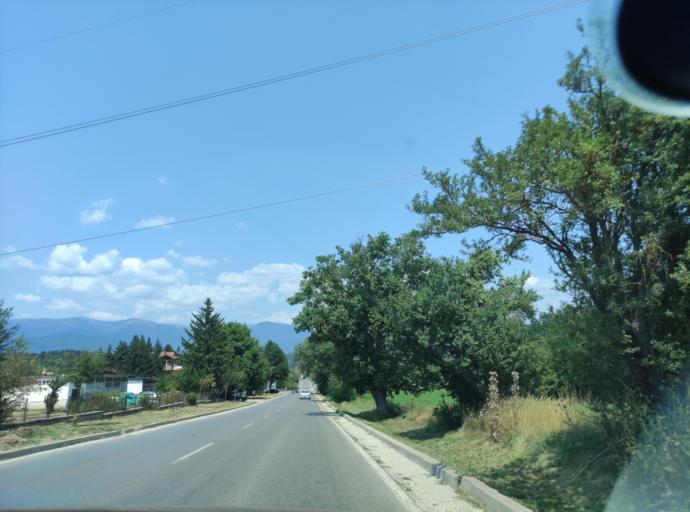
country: BG
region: Blagoevgrad
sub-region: Obshtina Razlog
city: Razlog
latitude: 41.8724
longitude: 23.4755
